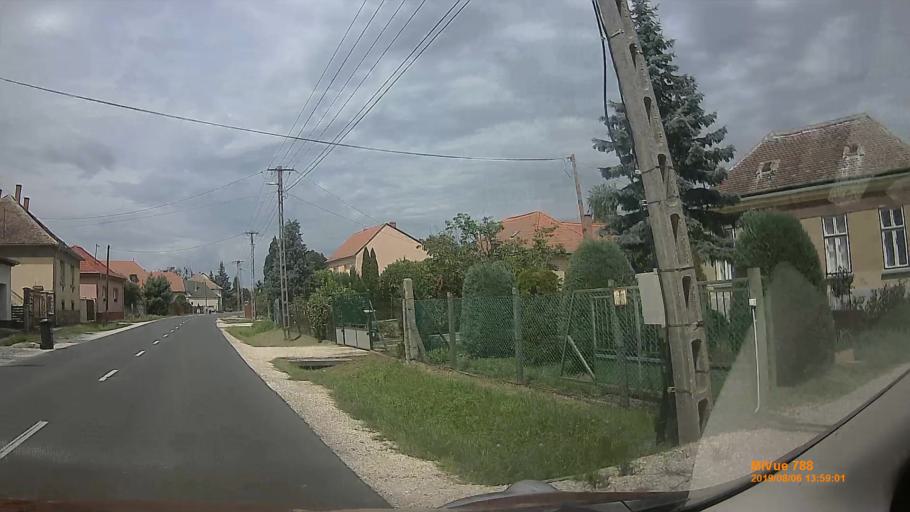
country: HU
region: Vas
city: Gencsapati
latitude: 47.2583
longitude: 16.6026
